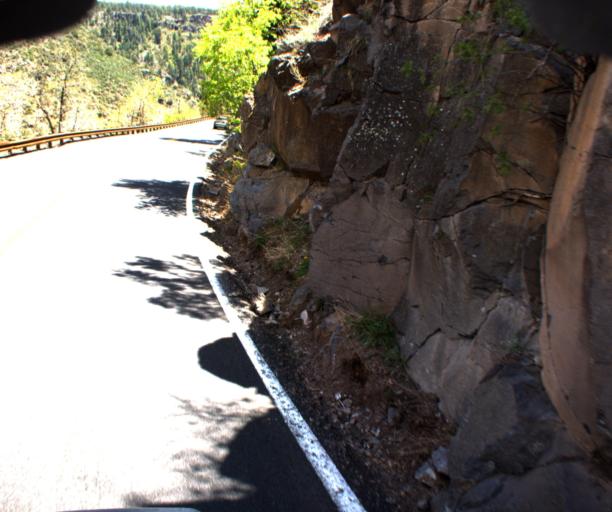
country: US
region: Arizona
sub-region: Coconino County
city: Kachina Village
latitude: 35.0283
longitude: -111.7405
